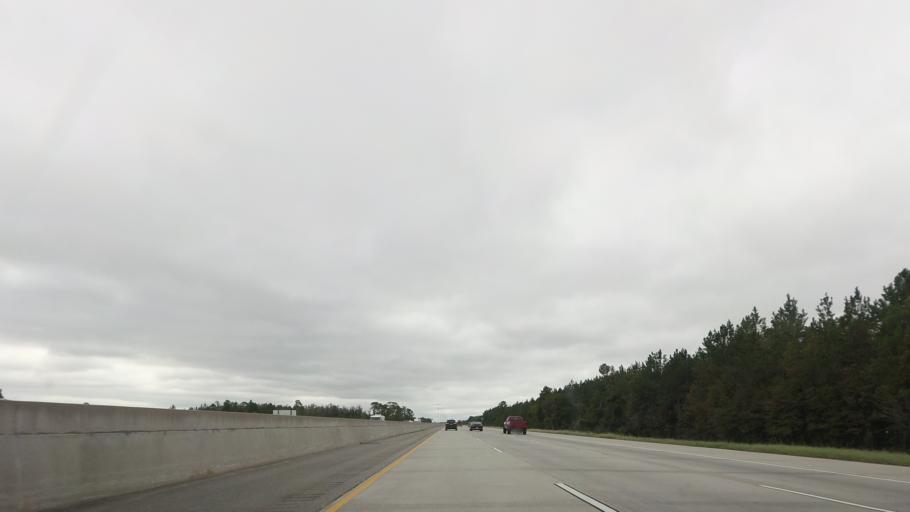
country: US
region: Georgia
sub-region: Cook County
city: Adel
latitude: 31.0953
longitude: -83.4187
